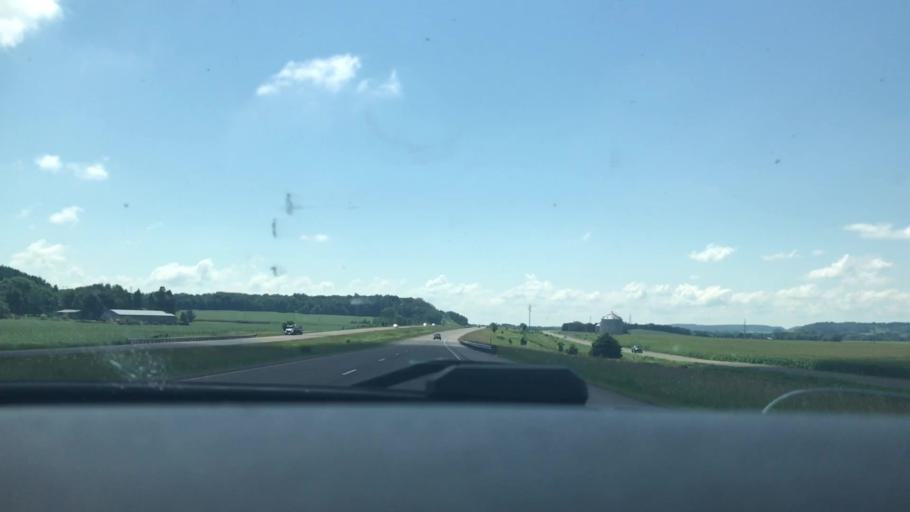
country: US
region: Wisconsin
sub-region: Chippewa County
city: Bloomer
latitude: 45.0369
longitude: -91.4555
